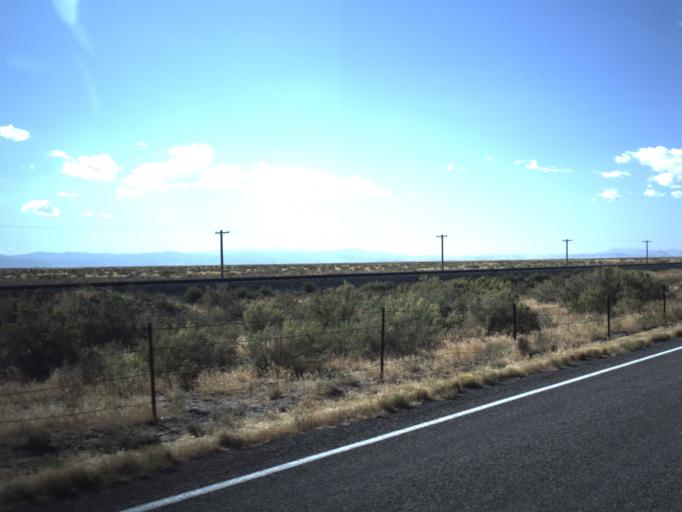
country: US
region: Utah
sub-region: Millard County
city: Delta
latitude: 39.2098
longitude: -112.6820
